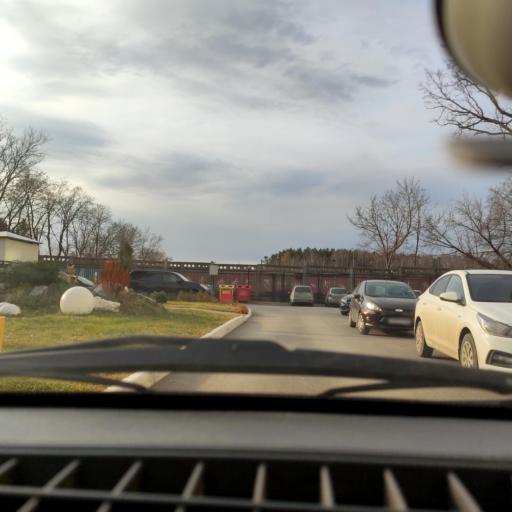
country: RU
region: Bashkortostan
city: Ufa
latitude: 54.7214
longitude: 56.0228
